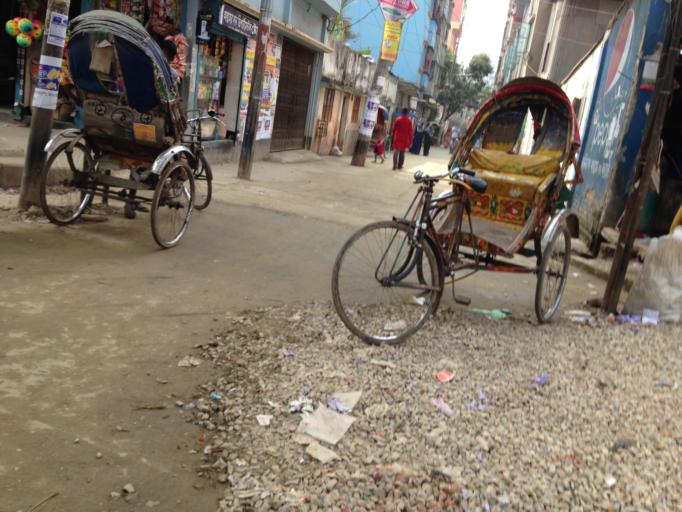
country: BD
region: Dhaka
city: Azimpur
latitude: 23.8040
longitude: 90.3477
